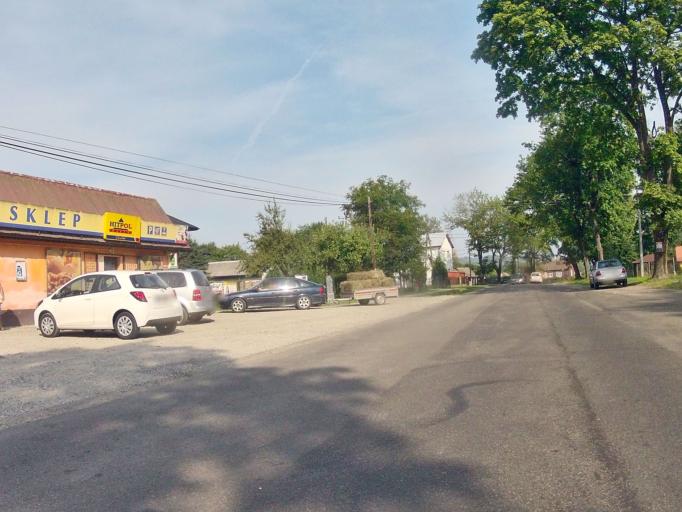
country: PL
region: Subcarpathian Voivodeship
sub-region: Powiat jasielski
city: Trzcinica
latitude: 49.7764
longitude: 21.4064
